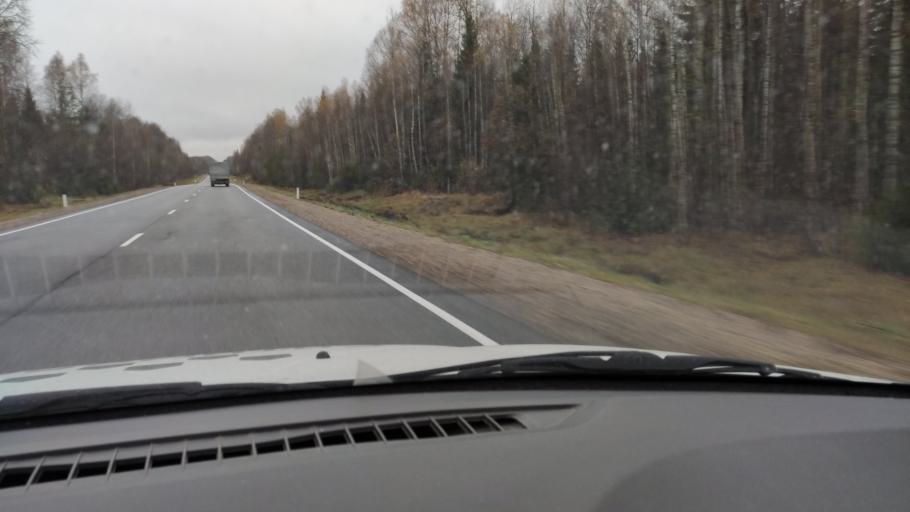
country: RU
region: Kirov
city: Chernaya Kholunitsa
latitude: 58.7840
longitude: 51.9057
